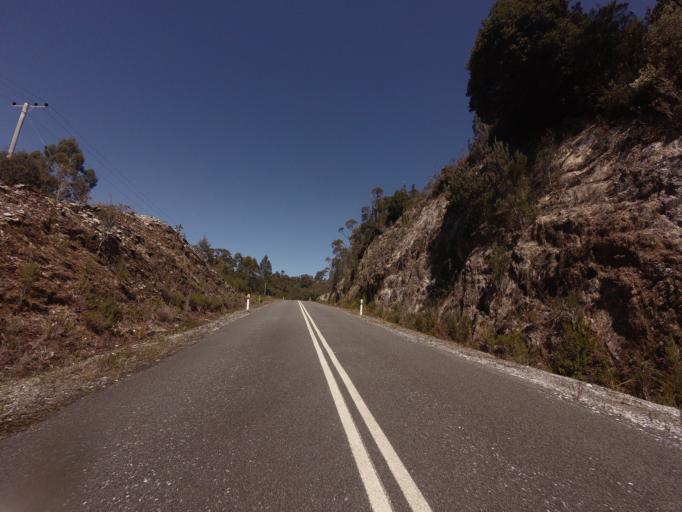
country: AU
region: Tasmania
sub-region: West Coast
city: Queenstown
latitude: -42.7597
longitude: 146.0036
